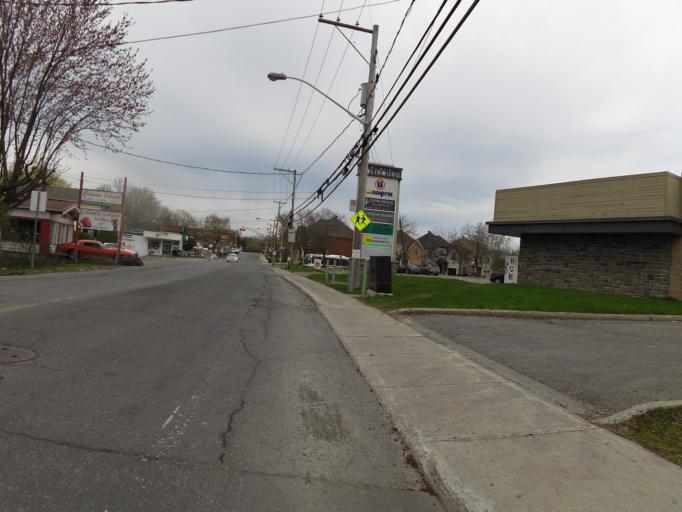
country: CA
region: Quebec
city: Dollard-Des Ormeaux
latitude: 45.5237
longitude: -73.8517
